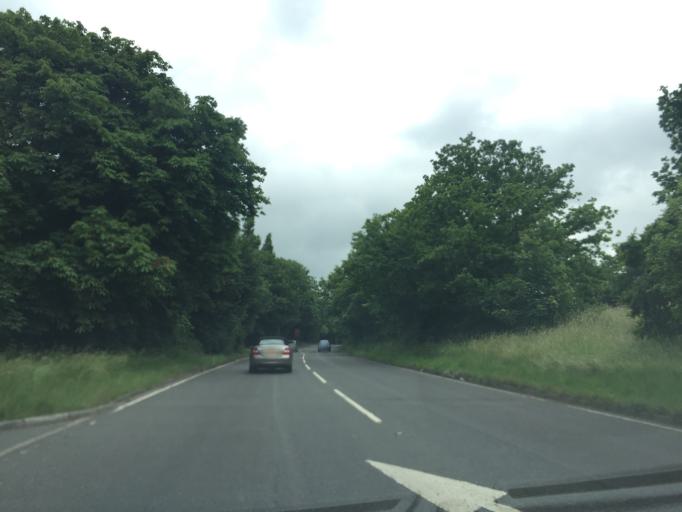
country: GB
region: England
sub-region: Essex
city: Theydon Bois
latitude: 51.6702
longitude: 0.1082
